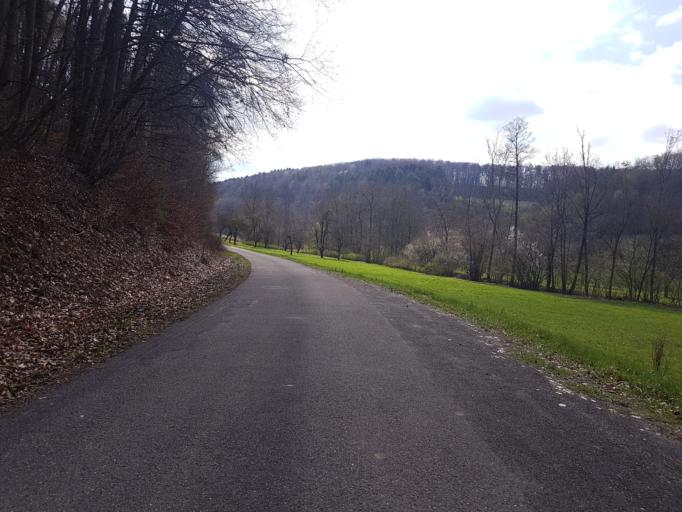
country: DE
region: Baden-Wuerttemberg
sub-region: Regierungsbezirk Stuttgart
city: Krautheim
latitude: 49.3536
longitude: 9.6122
